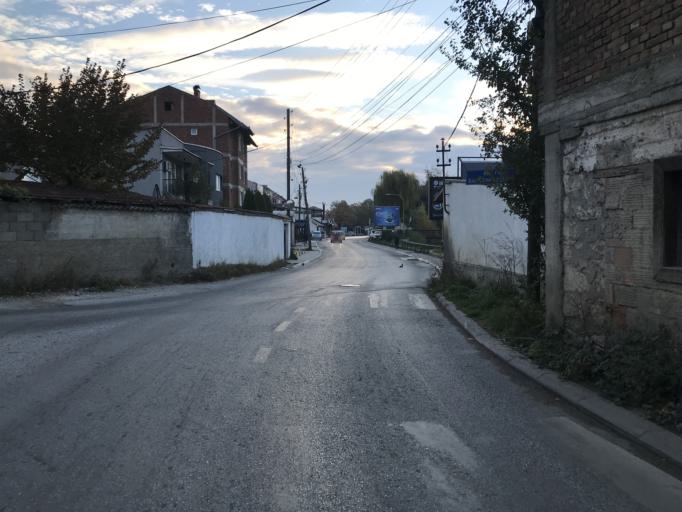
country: XK
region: Pec
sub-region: Komuna e Pejes
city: Peje
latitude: 42.6591
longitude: 20.2843
